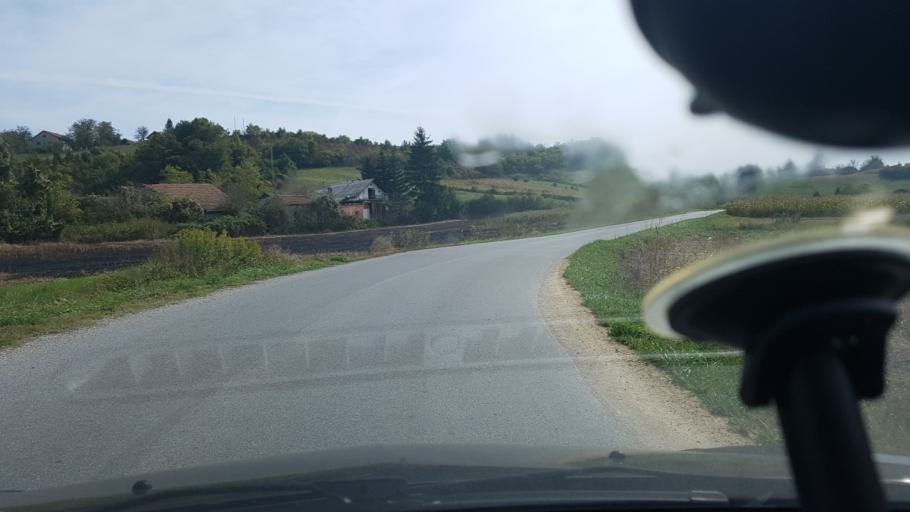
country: HR
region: Varazdinska
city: Remetinec
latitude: 46.1129
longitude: 16.2452
